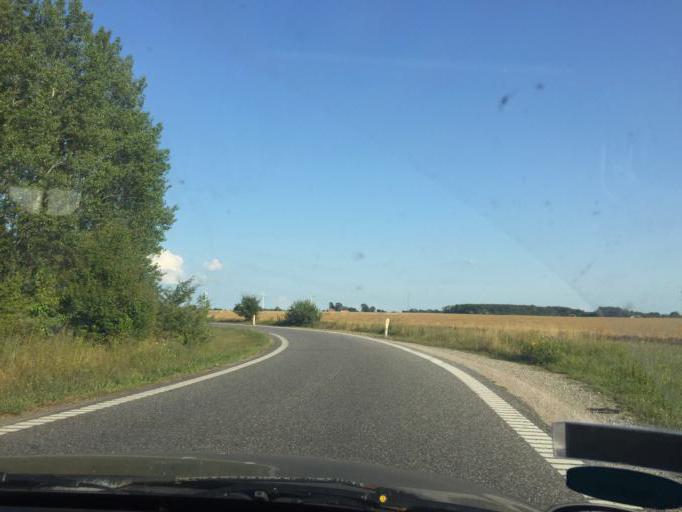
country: DK
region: Zealand
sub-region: Lolland Kommune
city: Maribo
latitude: 54.7884
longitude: 11.5629
